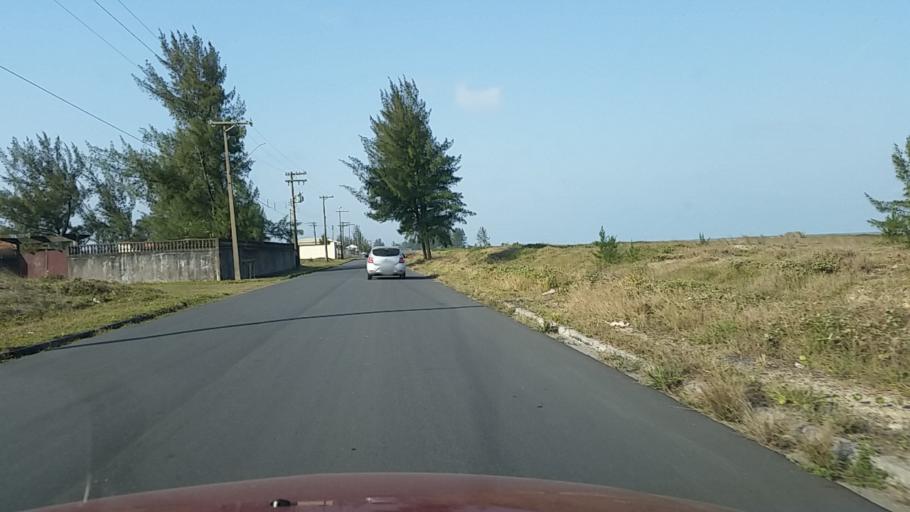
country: BR
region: Sao Paulo
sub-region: Iguape
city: Iguape
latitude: -24.8165
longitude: -47.6500
